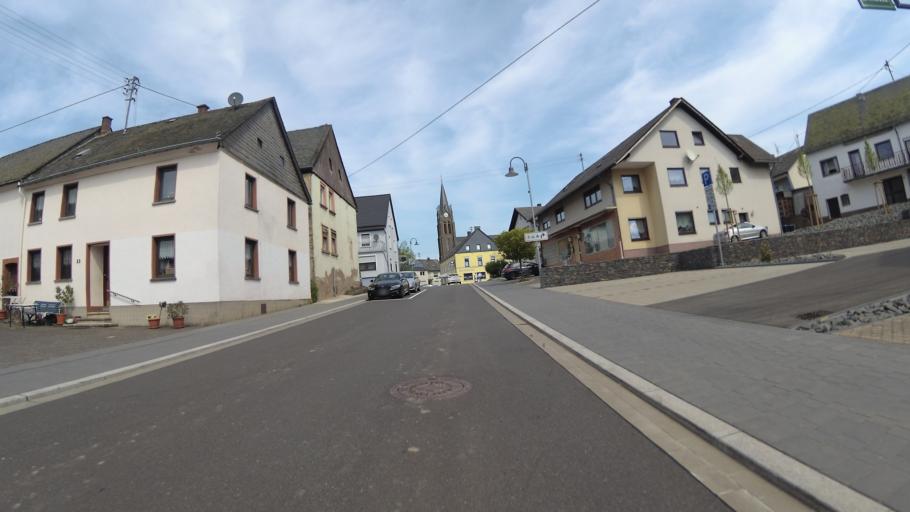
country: DE
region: Rheinland-Pfalz
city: Longkamp
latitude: 49.8563
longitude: 7.1154
